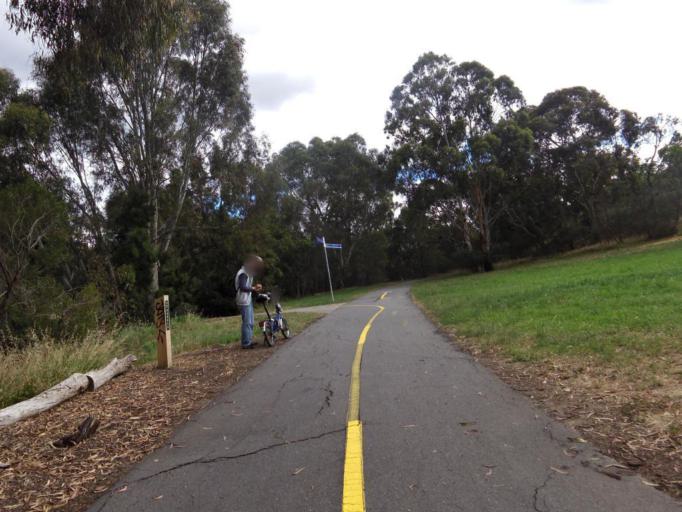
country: AU
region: Victoria
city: Heidelberg West
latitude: -37.7512
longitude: 145.0316
